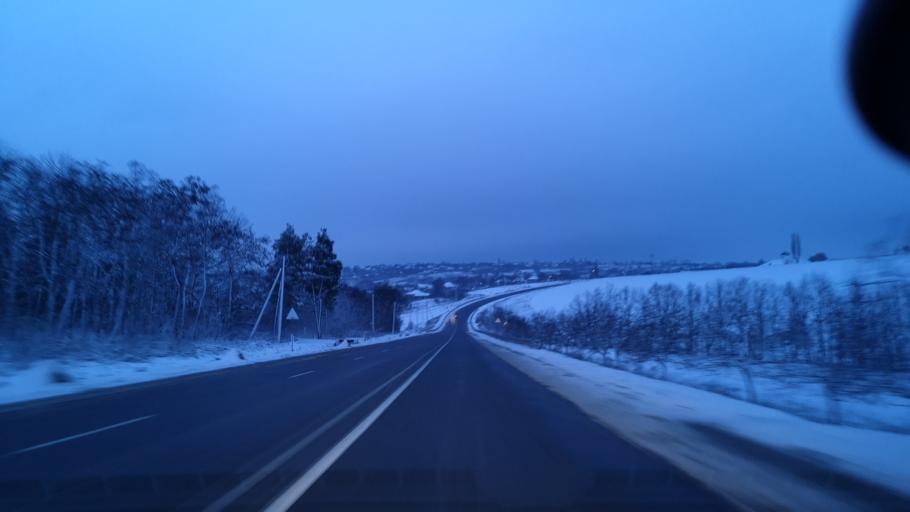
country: MD
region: Soldanesti
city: Soldanesti
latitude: 47.7080
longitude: 28.8471
